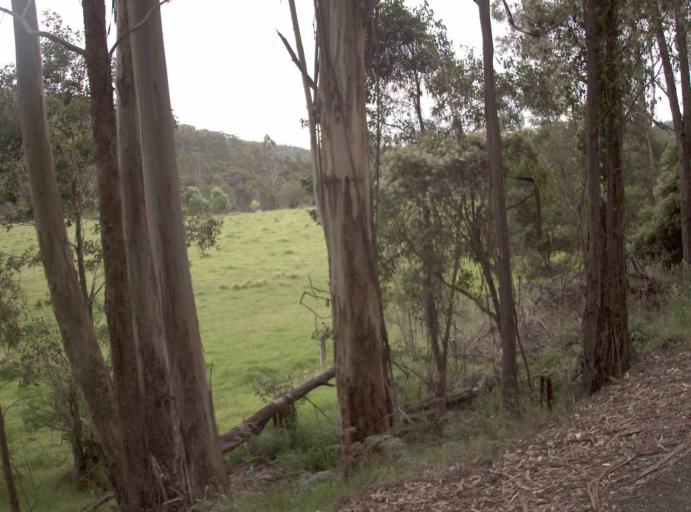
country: AU
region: New South Wales
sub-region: Bombala
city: Bombala
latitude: -37.4534
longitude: 149.1916
